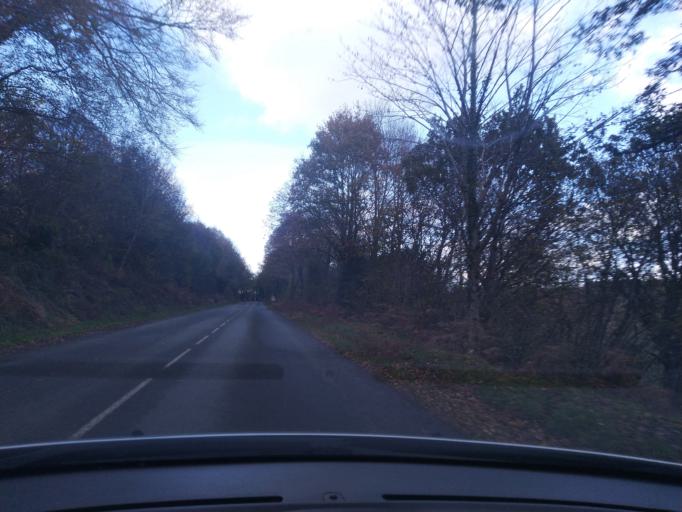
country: FR
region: Brittany
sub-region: Departement du Finistere
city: Plouigneau
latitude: 48.5692
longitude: -3.6394
